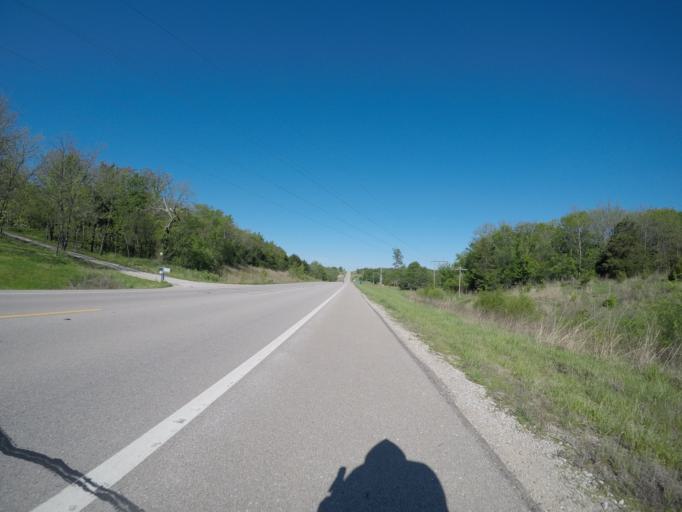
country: US
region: Kansas
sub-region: Douglas County
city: Lawrence
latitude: 38.9714
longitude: -95.4123
